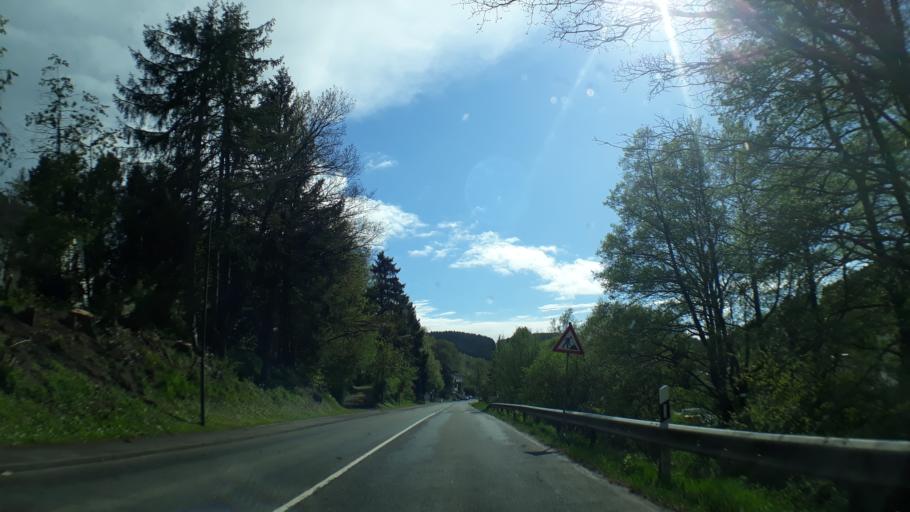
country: DE
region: North Rhine-Westphalia
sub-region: Regierungsbezirk Koln
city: Hellenthal
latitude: 50.4940
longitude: 6.4593
